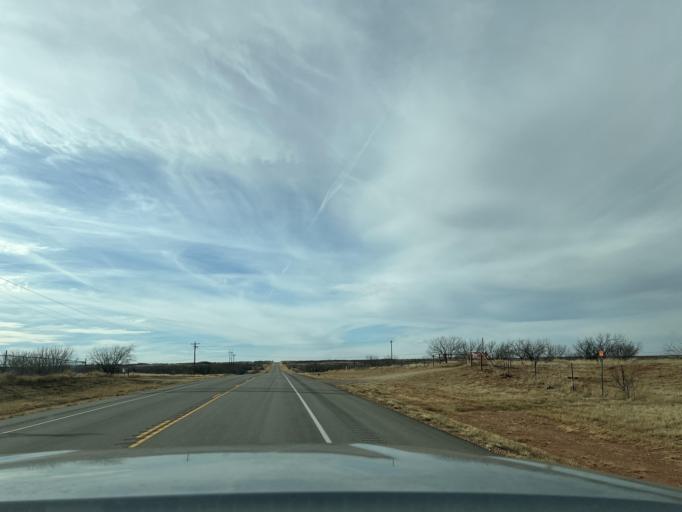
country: US
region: Texas
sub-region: Jones County
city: Anson
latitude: 32.7508
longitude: -99.7248
